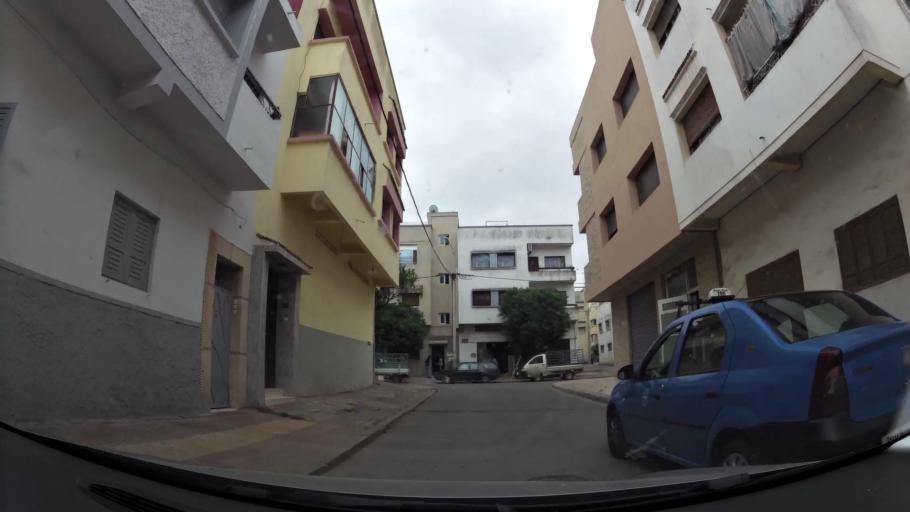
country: MA
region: Rabat-Sale-Zemmour-Zaer
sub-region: Rabat
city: Rabat
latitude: 33.9795
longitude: -6.8189
